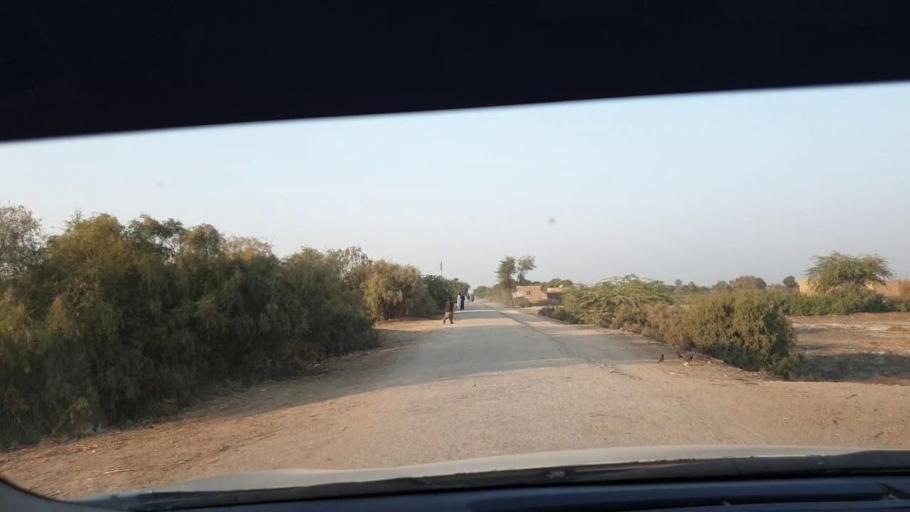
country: PK
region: Sindh
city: Berani
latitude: 25.8515
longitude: 68.8166
